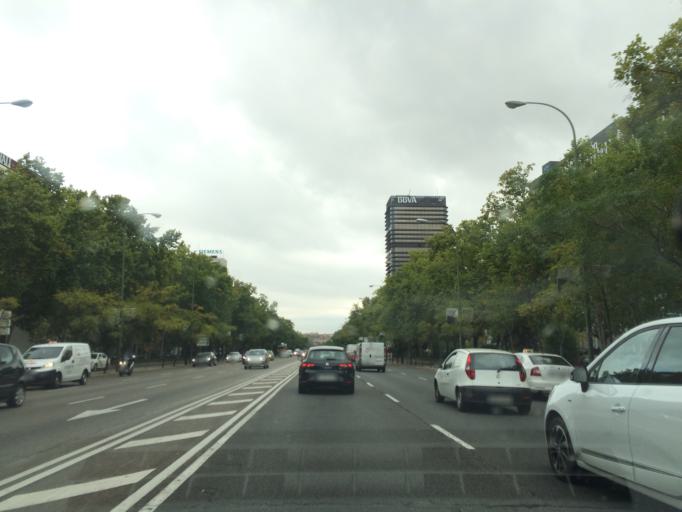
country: ES
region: Madrid
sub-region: Provincia de Madrid
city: Chamartin
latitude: 40.4513
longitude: -3.6908
